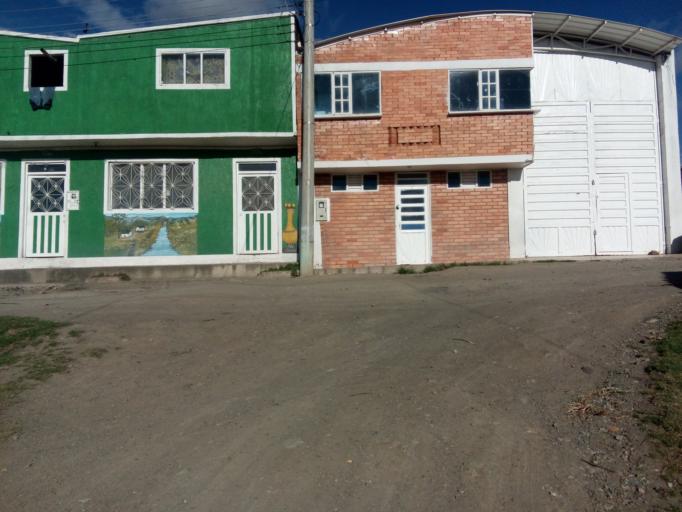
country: CO
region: Boyaca
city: Gameza
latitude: 5.8019
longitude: -72.8028
